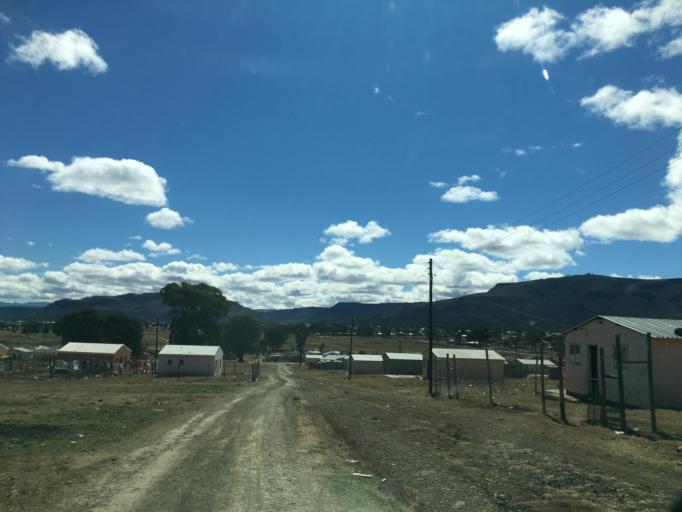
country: ZA
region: Eastern Cape
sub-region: Chris Hani District Municipality
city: Cala
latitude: -31.5427
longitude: 27.6831
